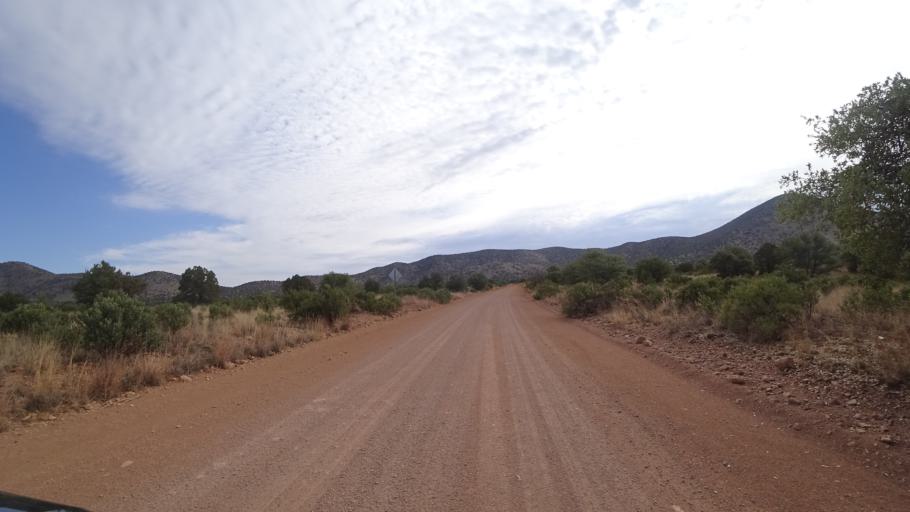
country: MX
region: Sonora
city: Santa Cruz
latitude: 31.4829
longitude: -110.5624
